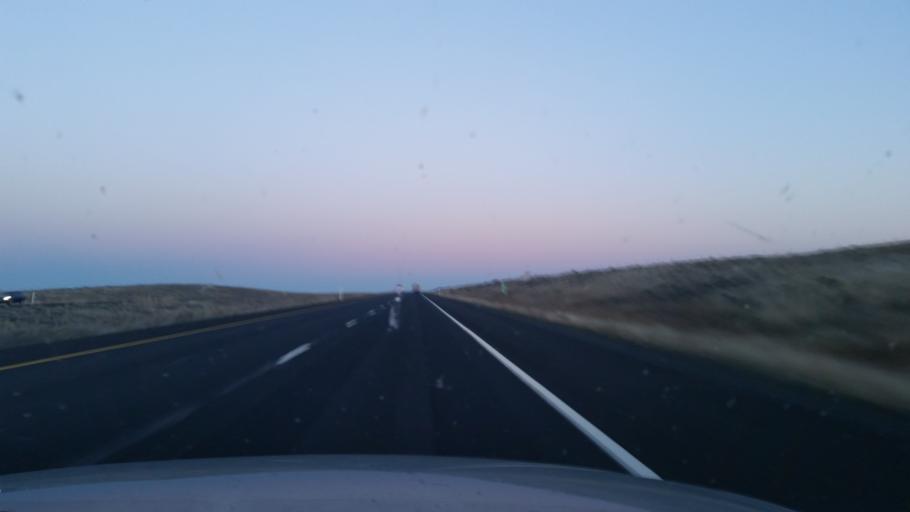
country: US
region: Washington
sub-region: Adams County
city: Ritzville
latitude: 47.1103
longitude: -118.5432
